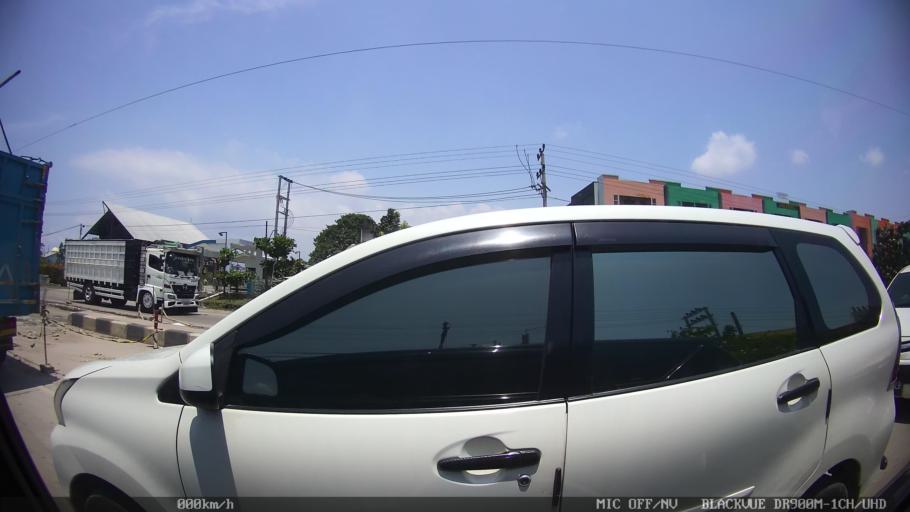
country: ID
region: Lampung
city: Kedaton
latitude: -5.3933
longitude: 105.2891
